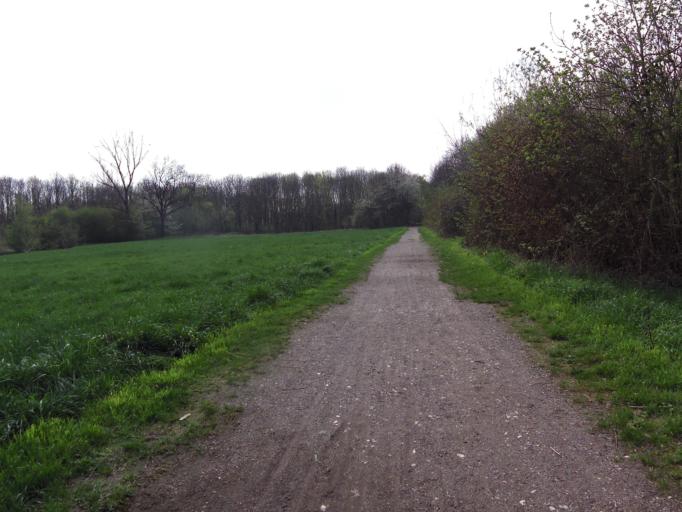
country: DE
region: Saxony
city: Markranstadt
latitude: 51.3192
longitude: 12.2563
